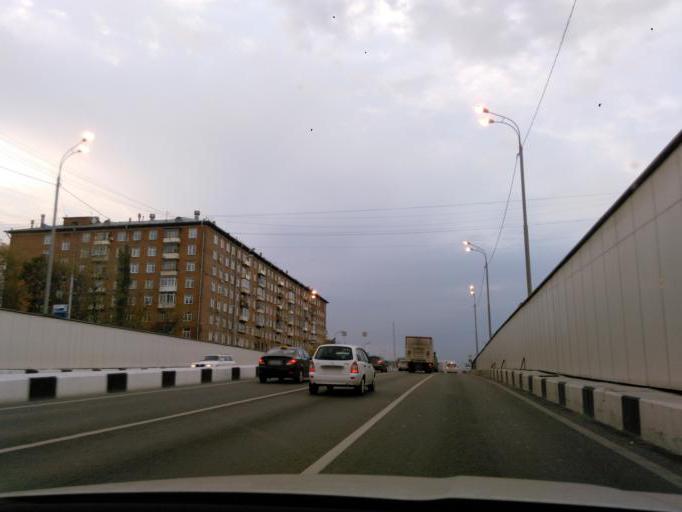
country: RU
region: Moscow
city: Likhobory
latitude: 55.8436
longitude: 37.5690
